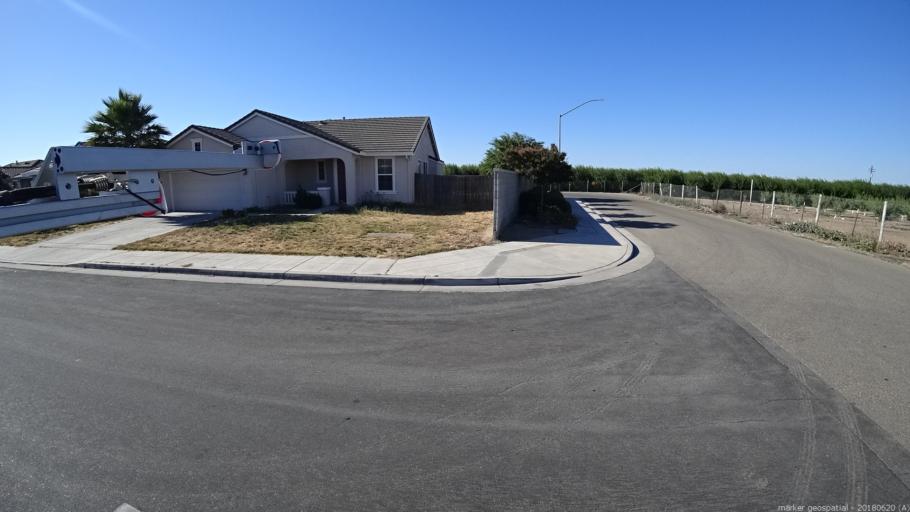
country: US
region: California
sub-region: Madera County
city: Parkwood
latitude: 36.9294
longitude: -120.0473
